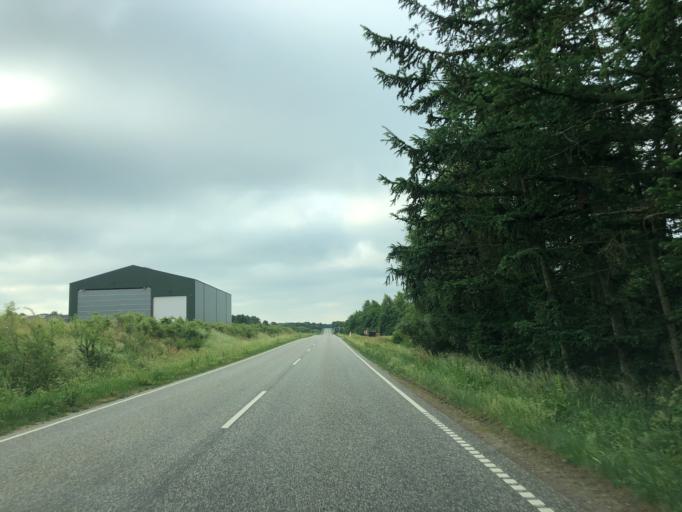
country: DK
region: Central Jutland
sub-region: Ikast-Brande Kommune
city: Brande
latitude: 55.9054
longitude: 9.1938
